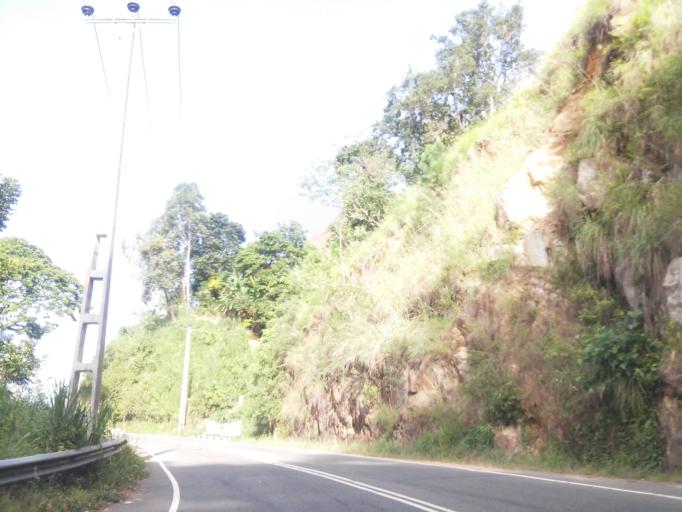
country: LK
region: Uva
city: Haputale
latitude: 6.7655
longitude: 80.8971
